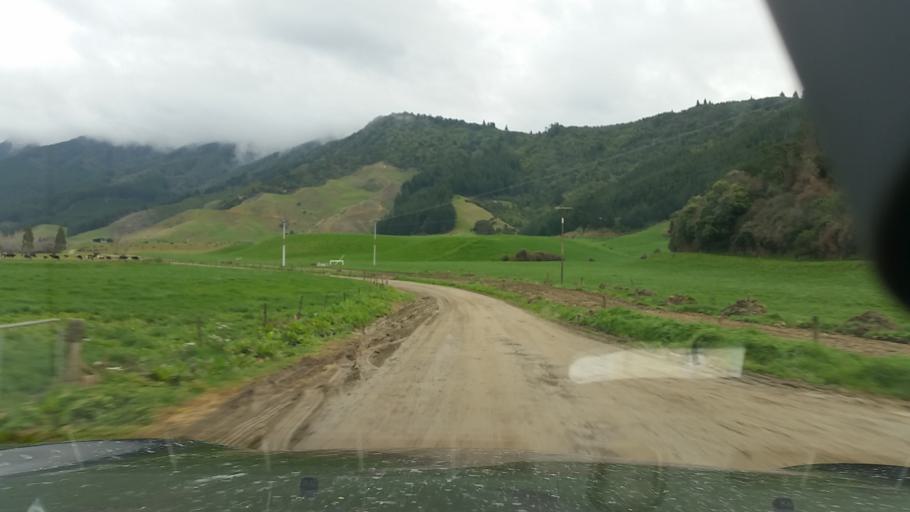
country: NZ
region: Marlborough
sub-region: Marlborough District
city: Picton
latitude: -41.2936
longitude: 173.8571
